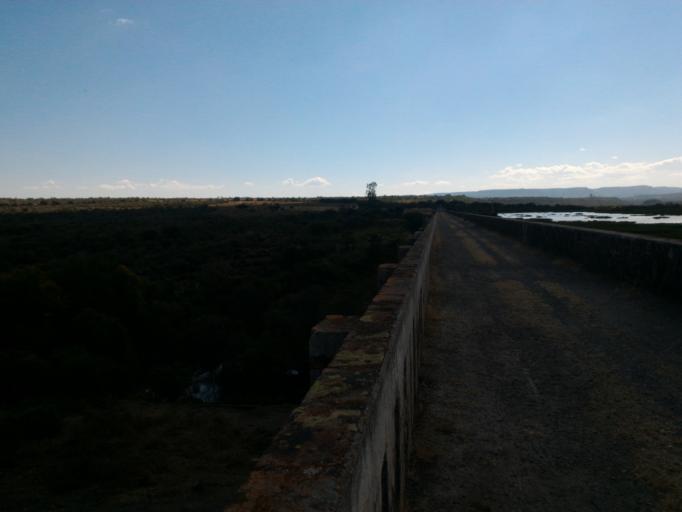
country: MX
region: Jalisco
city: San Diego de Alejandria
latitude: 20.8782
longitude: -102.0126
